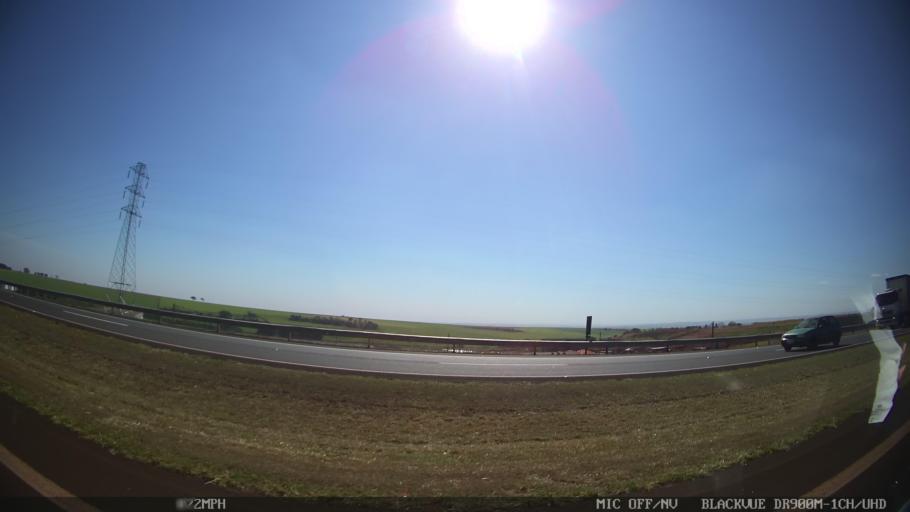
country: BR
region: Sao Paulo
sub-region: Ribeirao Preto
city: Ribeirao Preto
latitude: -21.1333
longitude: -47.8555
